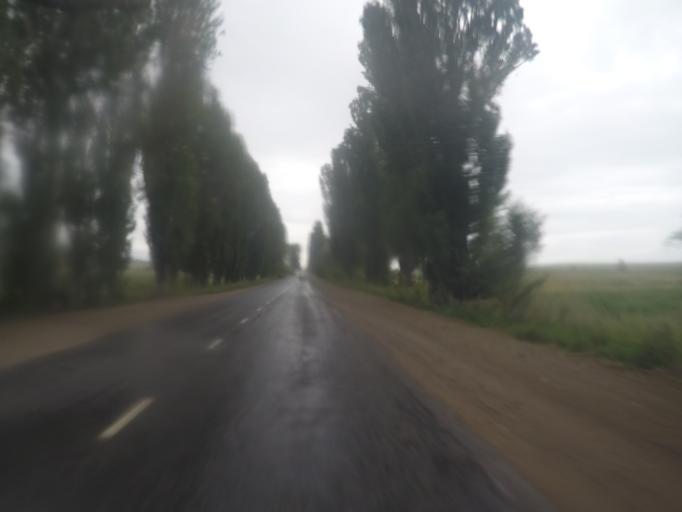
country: KG
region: Ysyk-Koel
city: Cholpon-Ata
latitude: 42.6951
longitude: 77.3924
